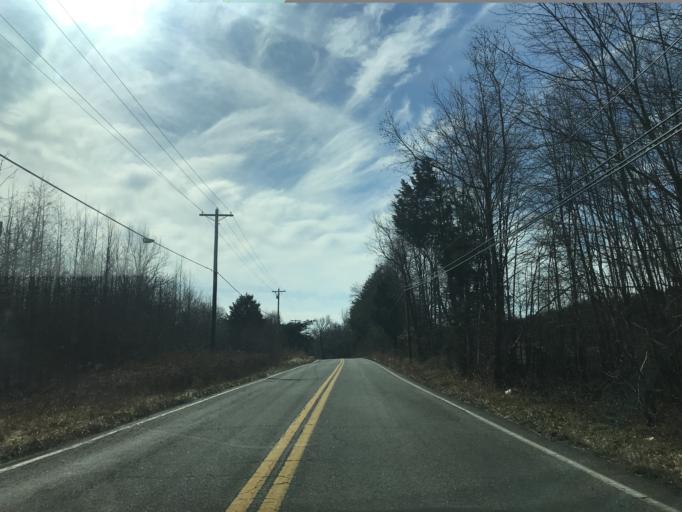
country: US
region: Maryland
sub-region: Charles County
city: Indian Head
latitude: 38.5486
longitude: -77.1296
